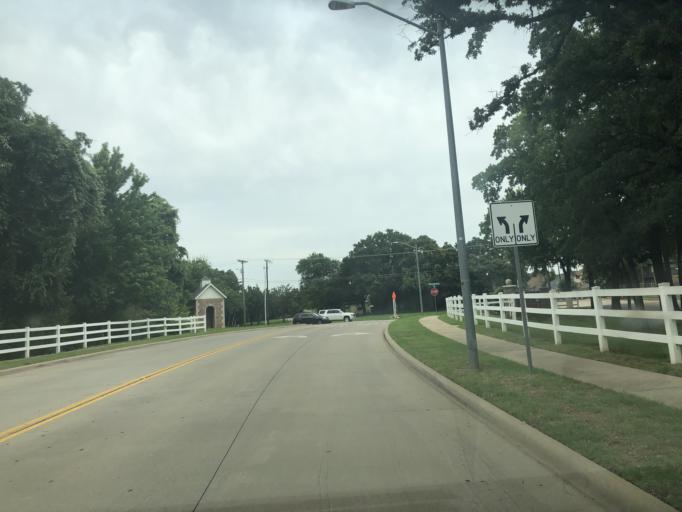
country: US
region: Texas
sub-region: Dallas County
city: Irving
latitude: 32.8034
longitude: -96.9920
